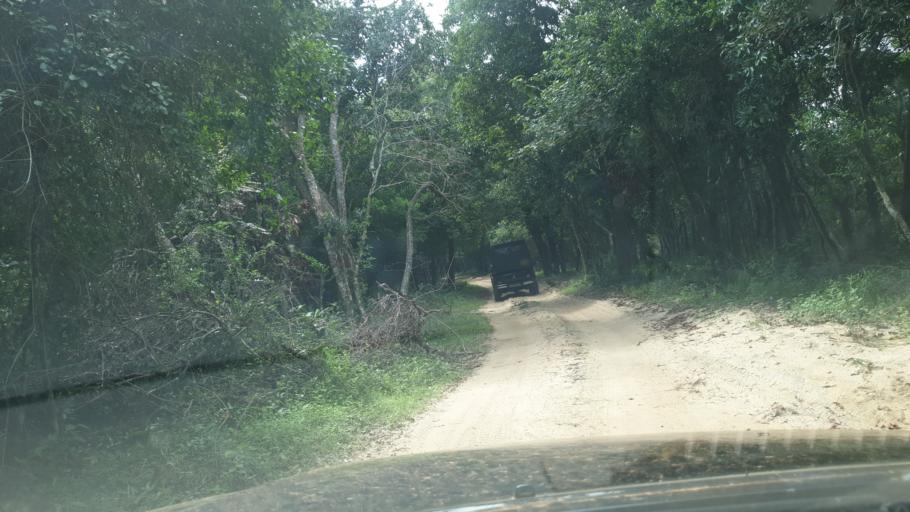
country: LK
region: North Western
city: Puttalam
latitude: 8.4136
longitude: 79.9920
